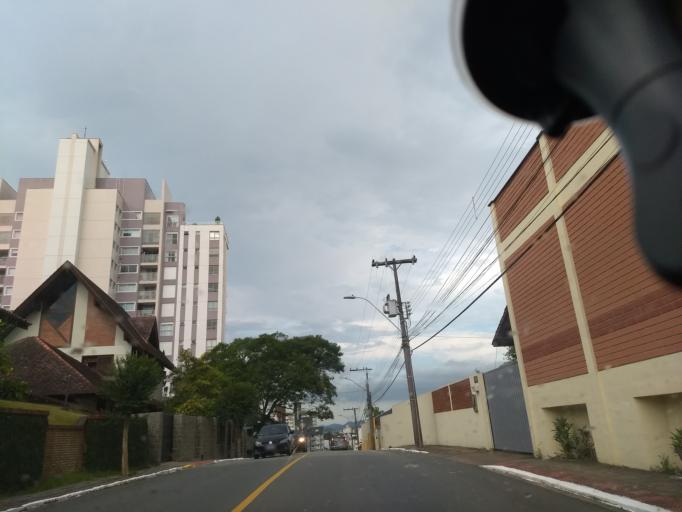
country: BR
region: Santa Catarina
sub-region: Jaragua Do Sul
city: Jaragua do Sul
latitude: -26.4836
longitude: -49.0892
